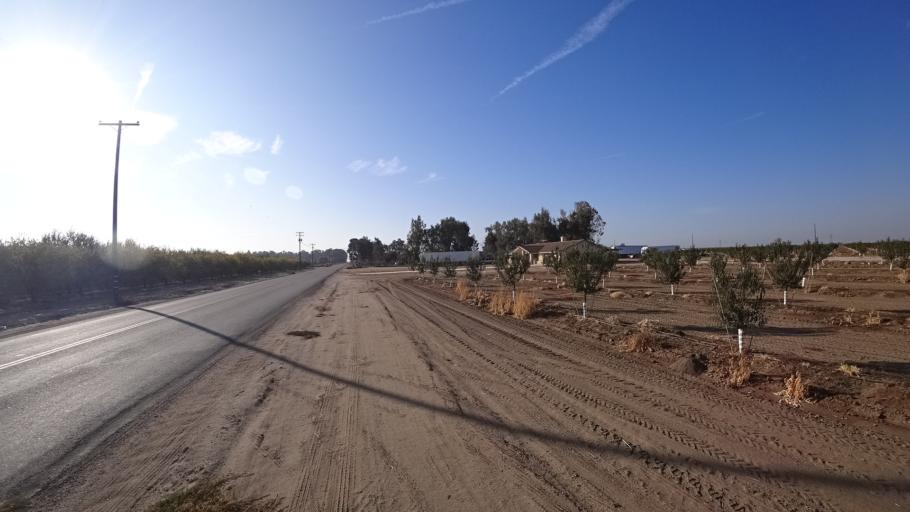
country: US
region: California
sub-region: Kern County
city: Greenfield
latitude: 35.2433
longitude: -119.0923
